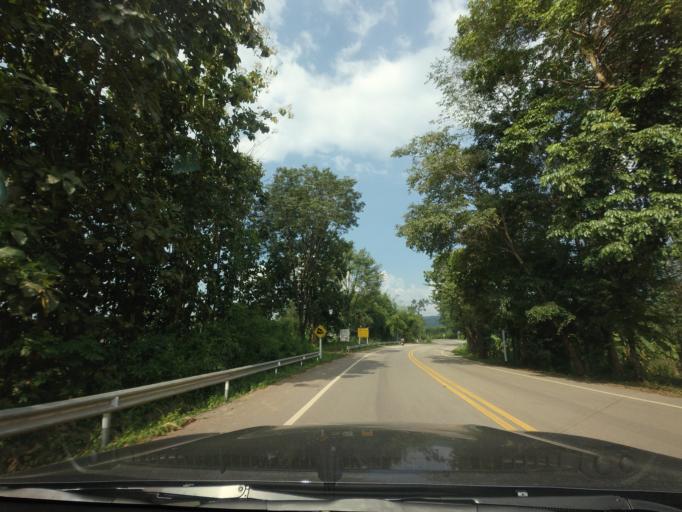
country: TH
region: Phitsanulok
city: Nakhon Thai
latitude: 17.0177
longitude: 100.9181
